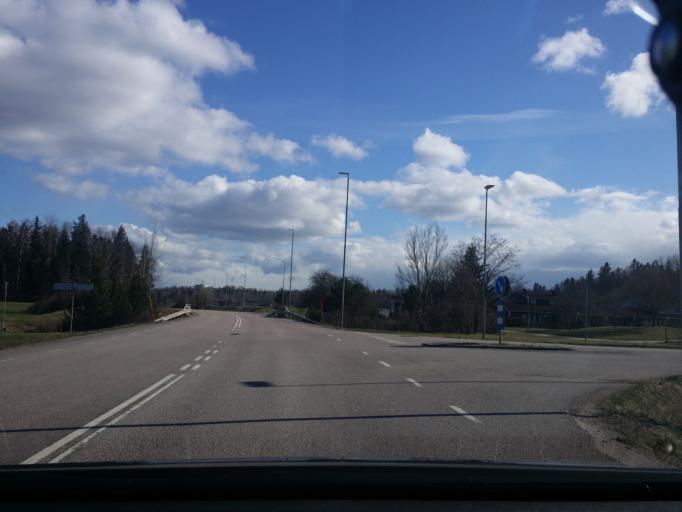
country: SE
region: Vaestmanland
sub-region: Sala Kommun
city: Sala
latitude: 59.9285
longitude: 16.5725
